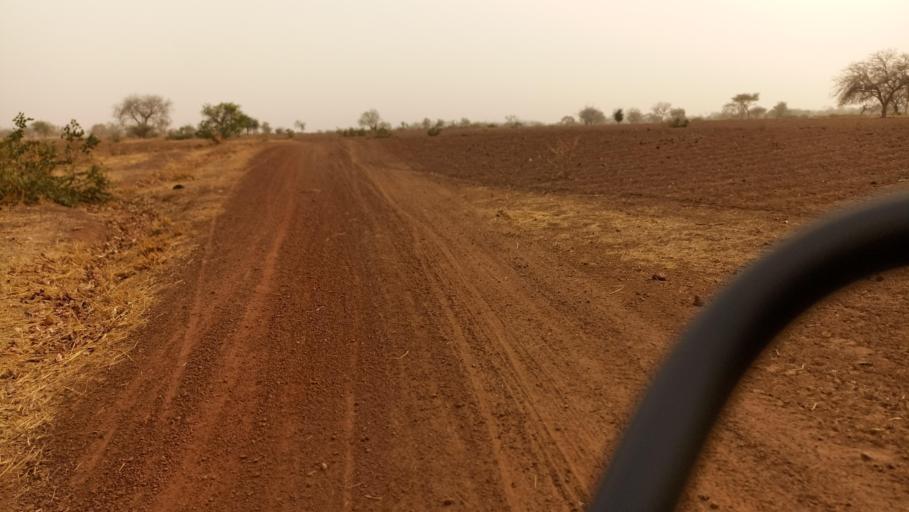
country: BF
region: Nord
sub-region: Province du Zondoma
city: Gourcy
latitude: 13.1484
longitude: -2.5967
